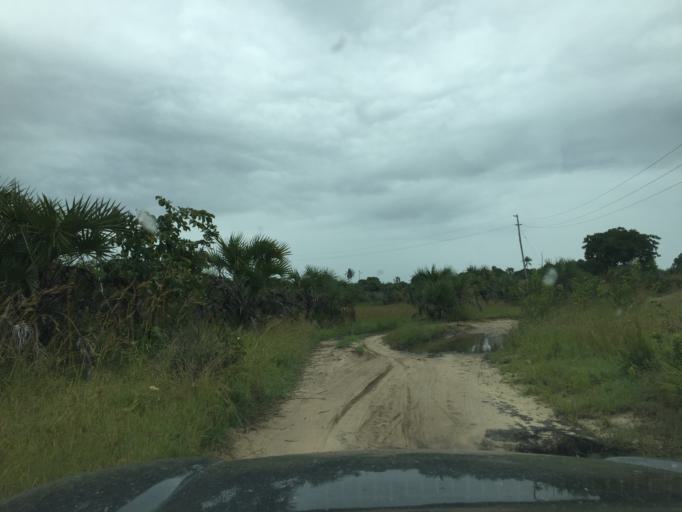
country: TZ
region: Pwani
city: Vikindu
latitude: -6.9394
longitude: 39.4933
